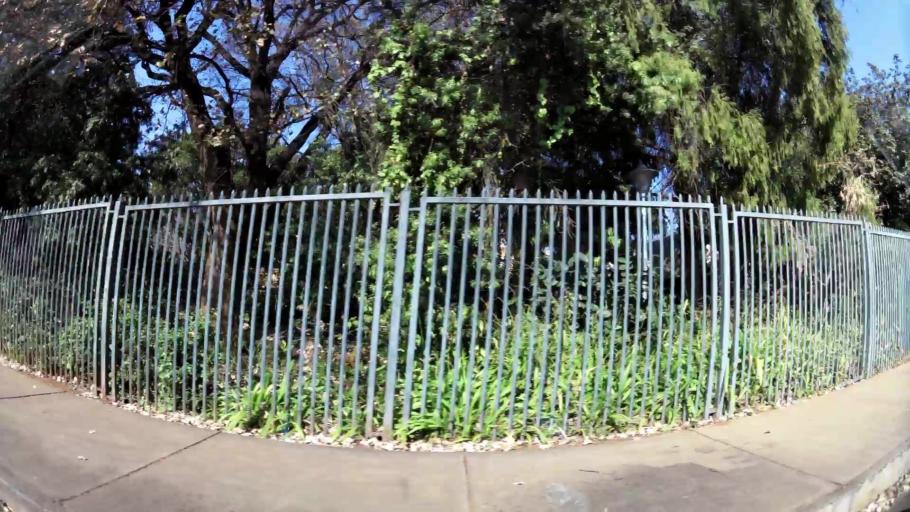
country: ZA
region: Gauteng
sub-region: City of Tshwane Metropolitan Municipality
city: Pretoria
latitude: -25.7514
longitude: 28.2291
